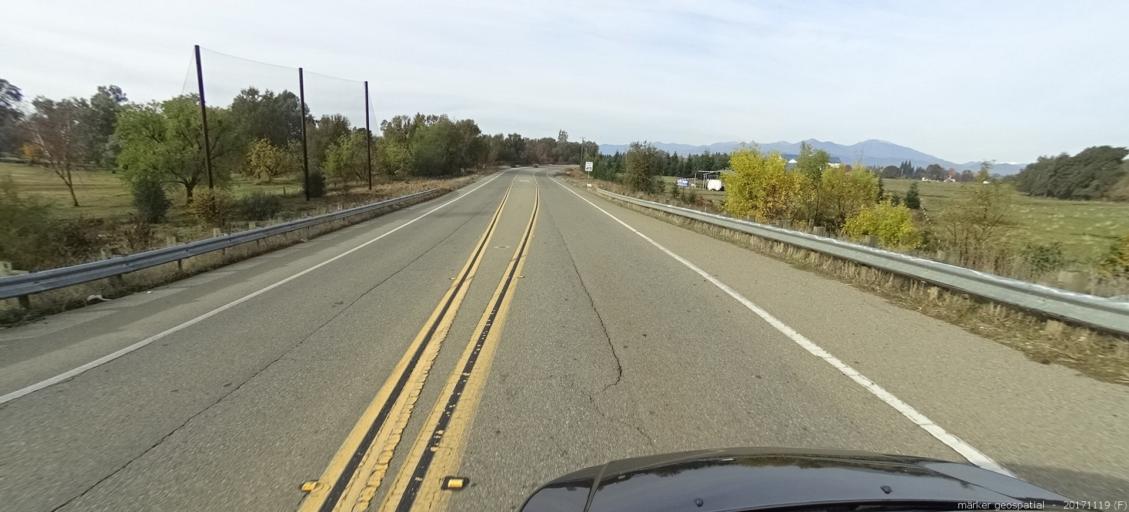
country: US
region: California
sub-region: Shasta County
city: Anderson
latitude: 40.5087
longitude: -122.3174
